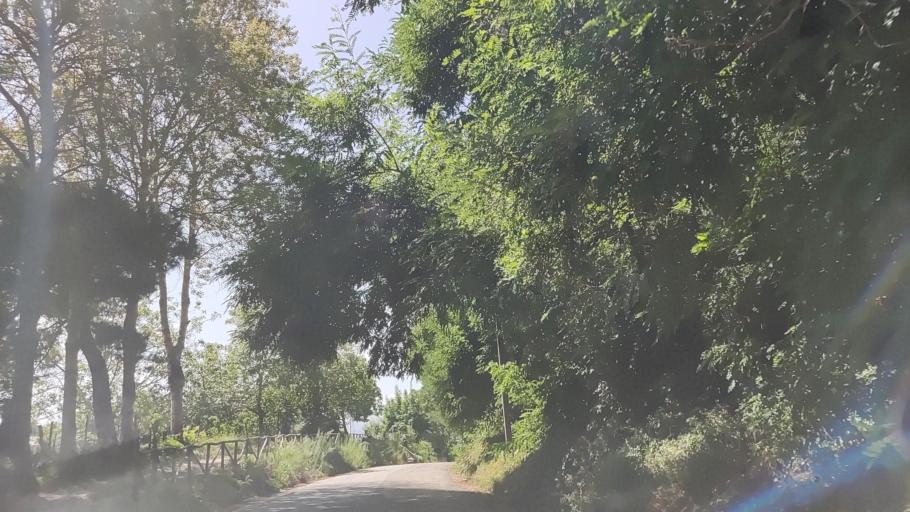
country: IT
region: Calabria
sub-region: Provincia di Reggio Calabria
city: Seminara
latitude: 38.3386
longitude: 15.8455
